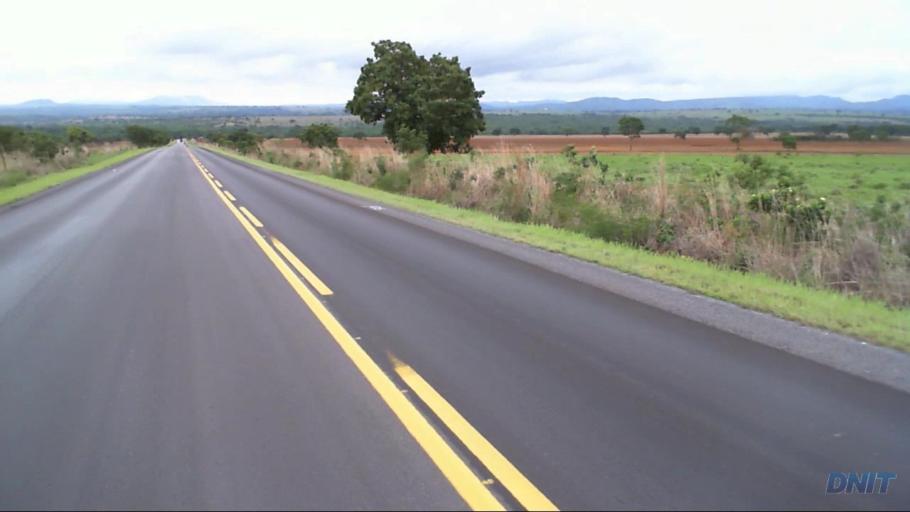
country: BR
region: Goias
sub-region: Padre Bernardo
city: Padre Bernardo
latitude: -15.2201
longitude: -48.5345
